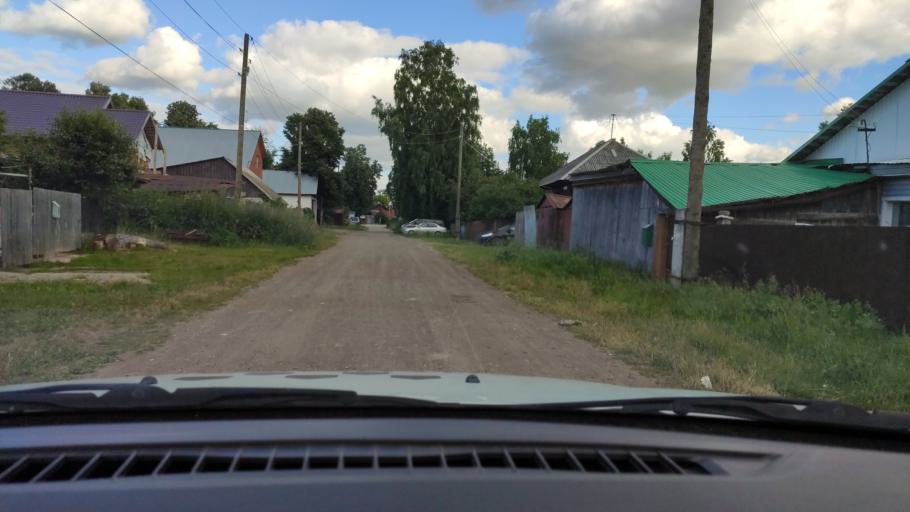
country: RU
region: Perm
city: Kondratovo
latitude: 57.9642
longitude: 56.1335
